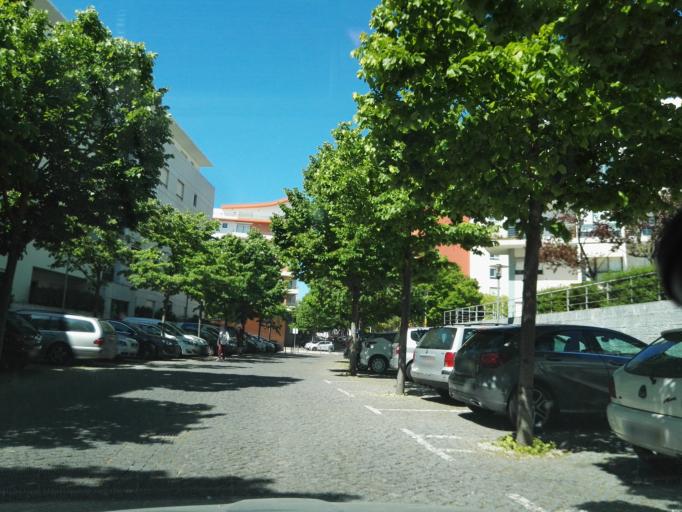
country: PT
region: Lisbon
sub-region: Loures
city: Moscavide
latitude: 38.7818
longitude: -9.0936
